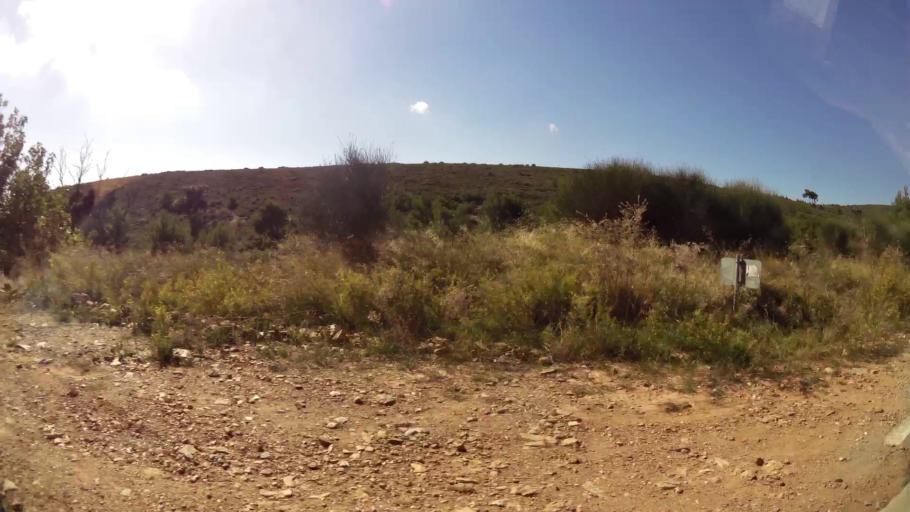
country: GR
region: Attica
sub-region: Nomarchia Anatolikis Attikis
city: Dioni
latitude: 38.0287
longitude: 23.9226
